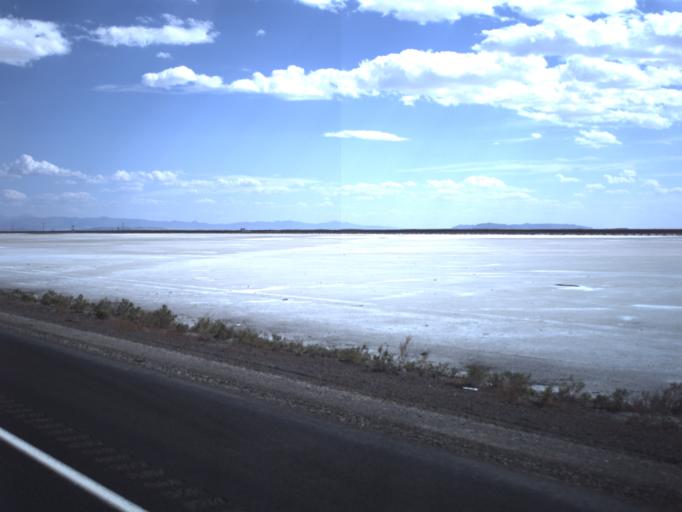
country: US
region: Utah
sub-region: Tooele County
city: Wendover
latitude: 40.7330
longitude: -113.5911
